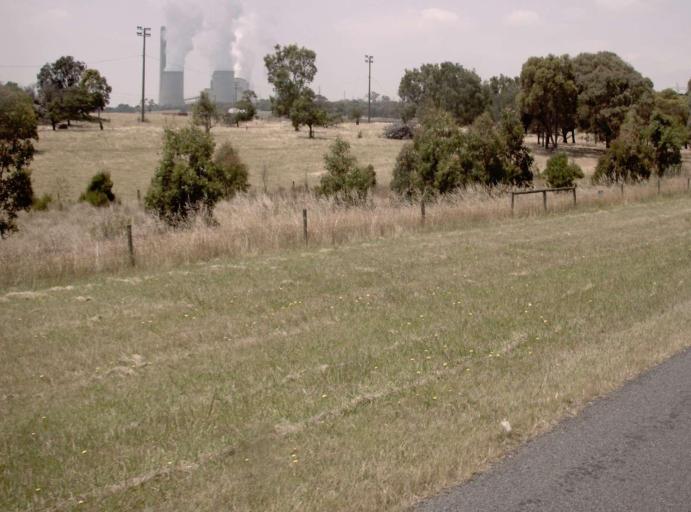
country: AU
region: Victoria
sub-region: Latrobe
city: Traralgon
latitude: -38.2452
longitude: 146.5465
